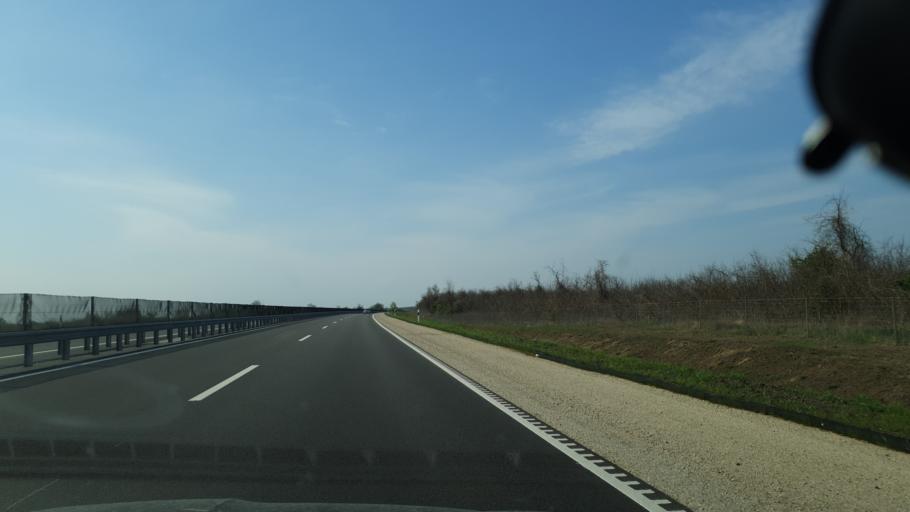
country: HU
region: Pest
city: Gomba
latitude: 47.3382
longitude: 19.5056
